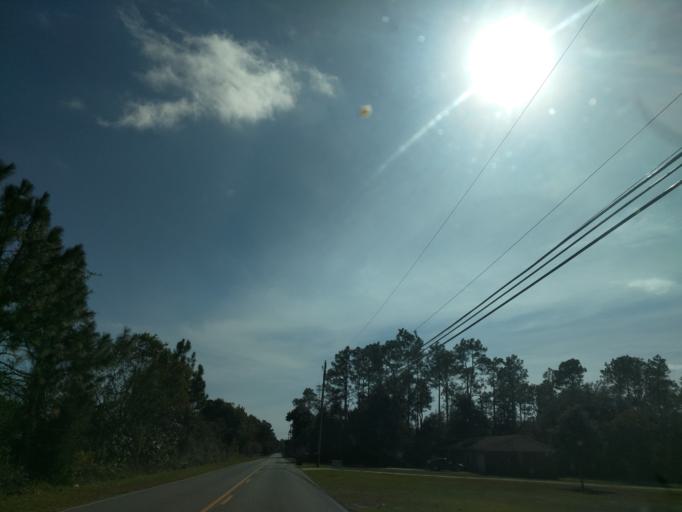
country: US
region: Florida
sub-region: Escambia County
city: Cantonment
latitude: 30.5432
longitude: -87.4059
